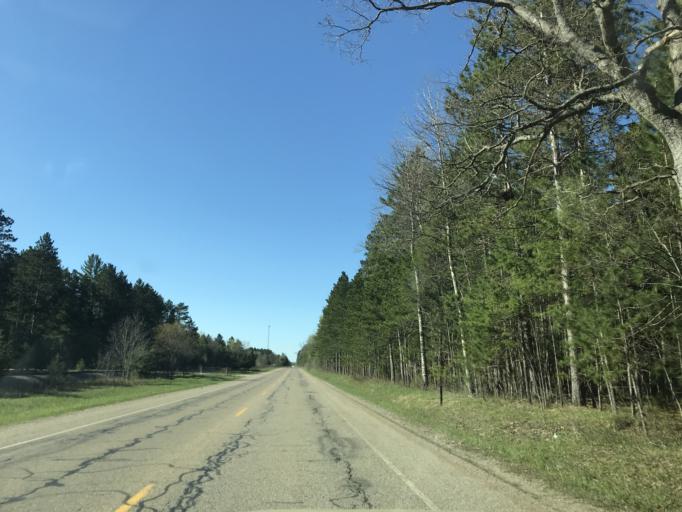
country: US
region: Michigan
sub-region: Crawford County
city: Grayling
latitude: 44.7286
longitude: -84.7483
